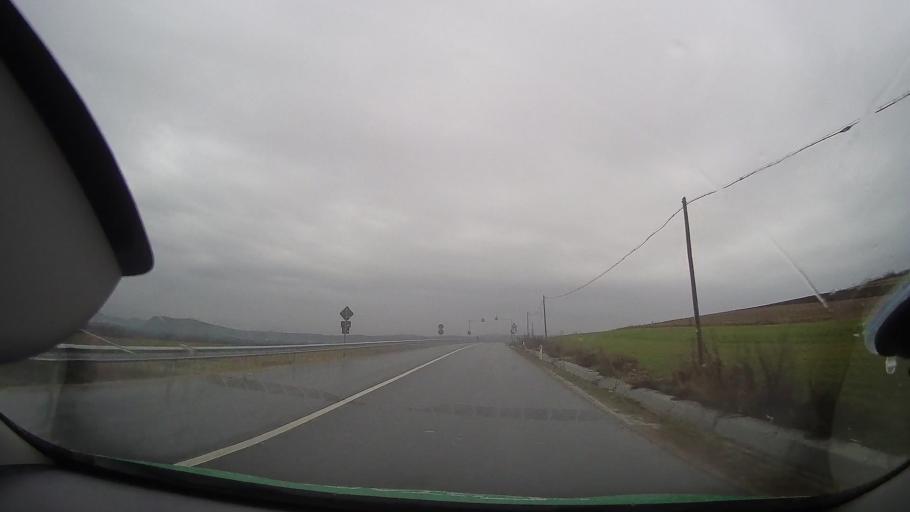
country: RO
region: Bihor
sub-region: Comuna Pocola
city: Pocola
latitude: 46.6821
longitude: 22.3094
